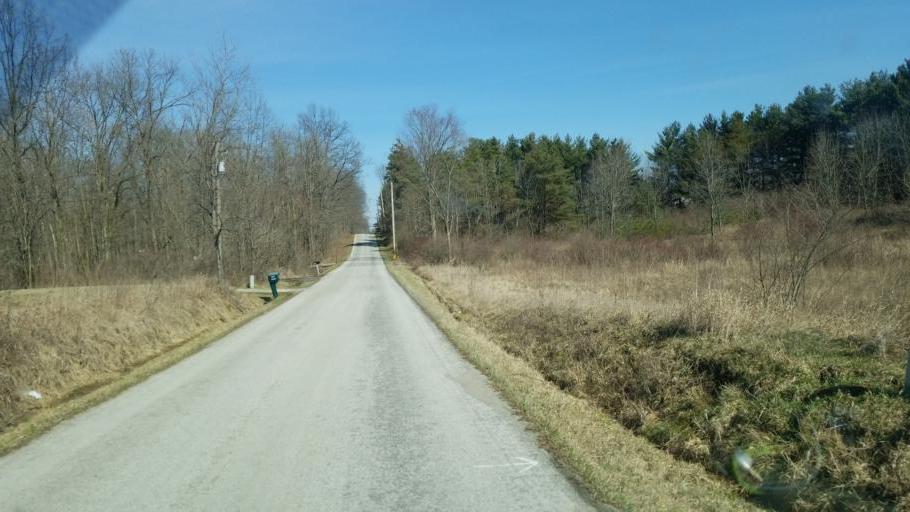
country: US
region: Ohio
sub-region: Wayne County
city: West Salem
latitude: 41.0021
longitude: -82.2420
